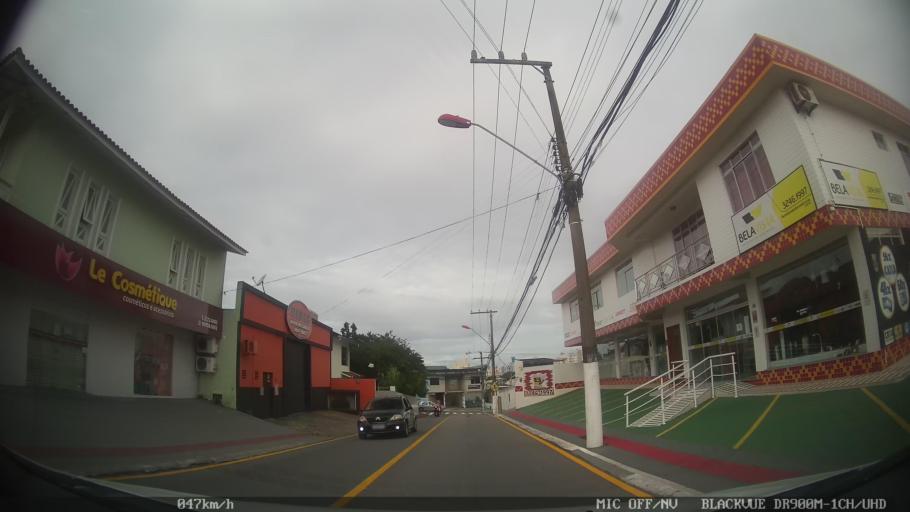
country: BR
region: Santa Catarina
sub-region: Sao Jose
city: Campinas
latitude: -27.5777
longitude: -48.6214
